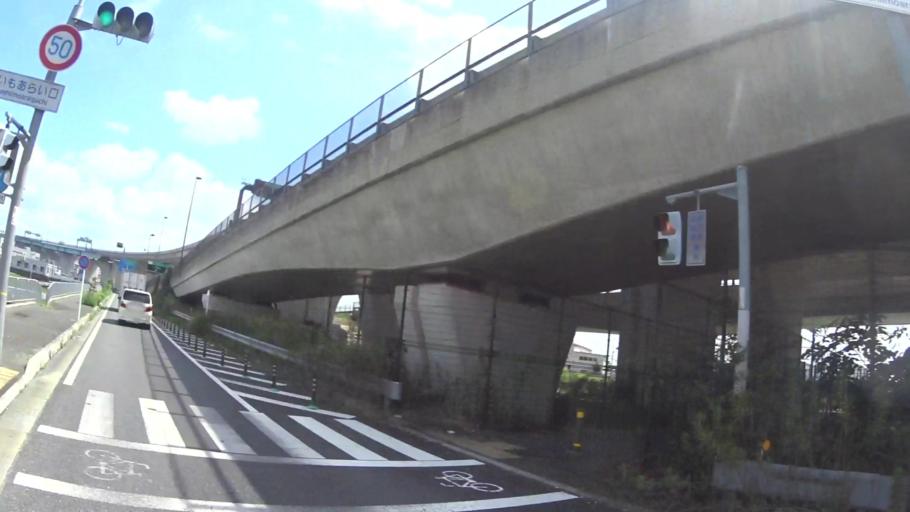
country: JP
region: Kyoto
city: Yawata
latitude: 34.8995
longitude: 135.7399
